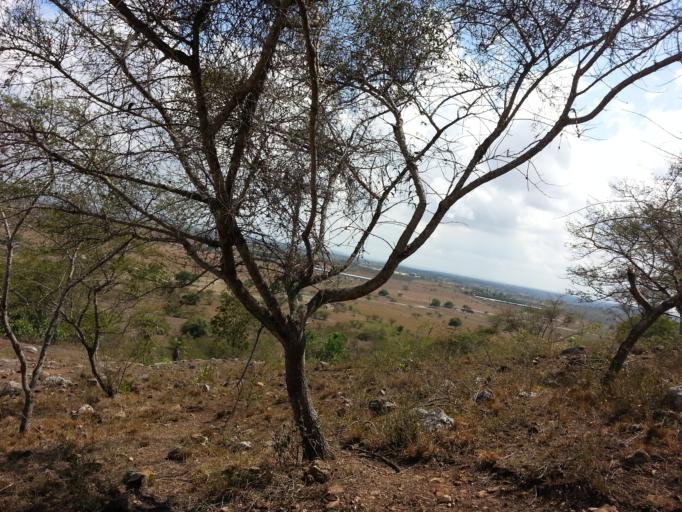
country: BR
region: Bahia
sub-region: Cruz Das Almas
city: Cruz das Almas
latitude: -12.5976
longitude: -39.1925
